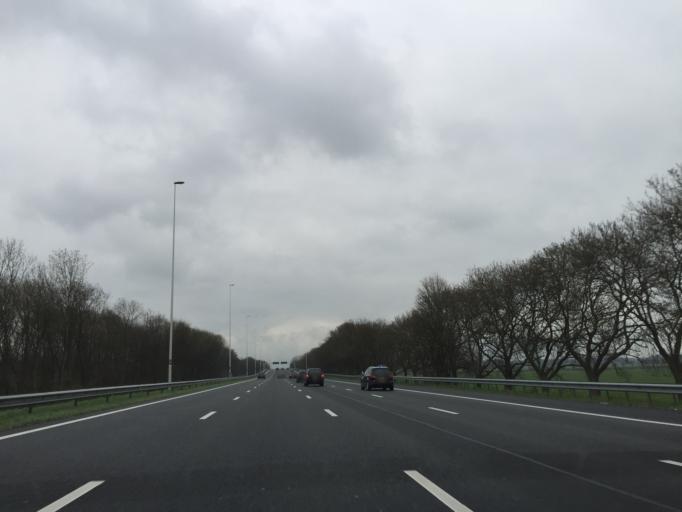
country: NL
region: Utrecht
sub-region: Gemeente Woerden
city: Woerden
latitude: 52.0694
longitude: 4.8642
